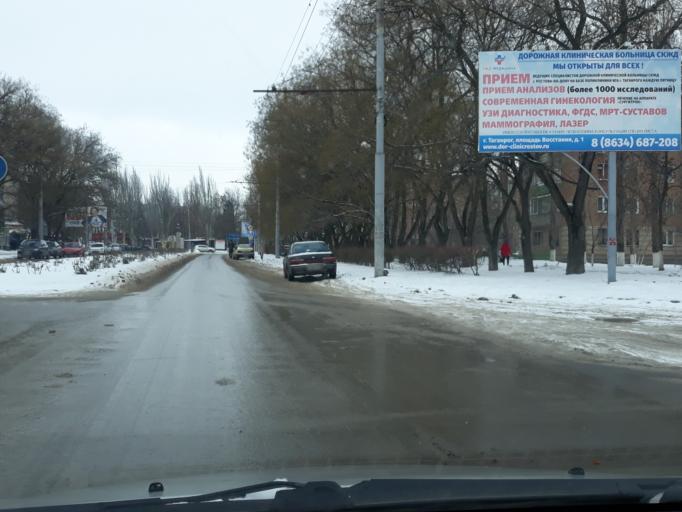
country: RU
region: Rostov
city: Taganrog
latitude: 47.2599
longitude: 38.9180
